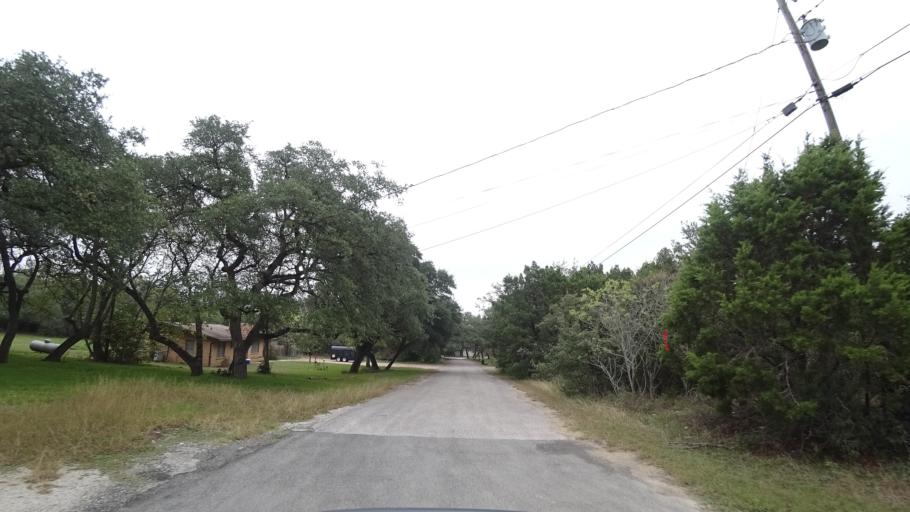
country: US
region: Texas
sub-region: Travis County
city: Barton Creek
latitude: 30.2322
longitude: -97.8956
